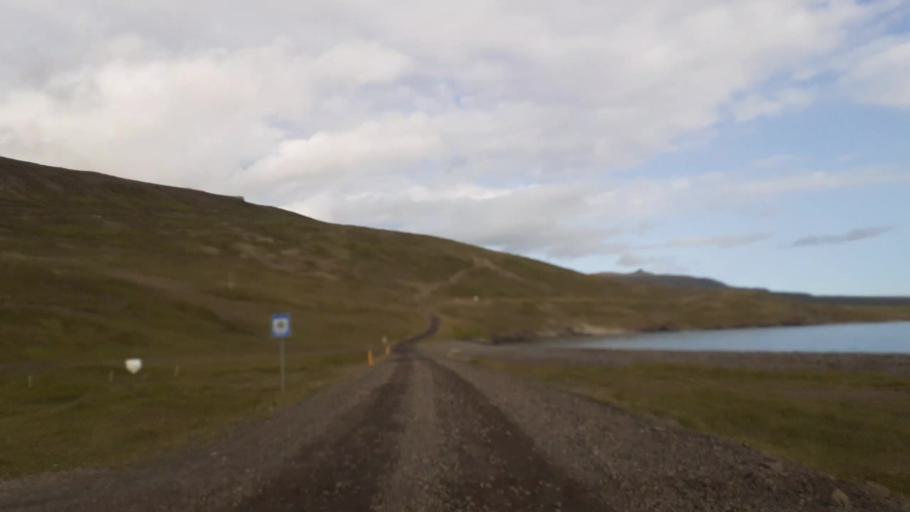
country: IS
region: East
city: Eskifjoerdur
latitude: 65.0352
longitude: -13.8716
